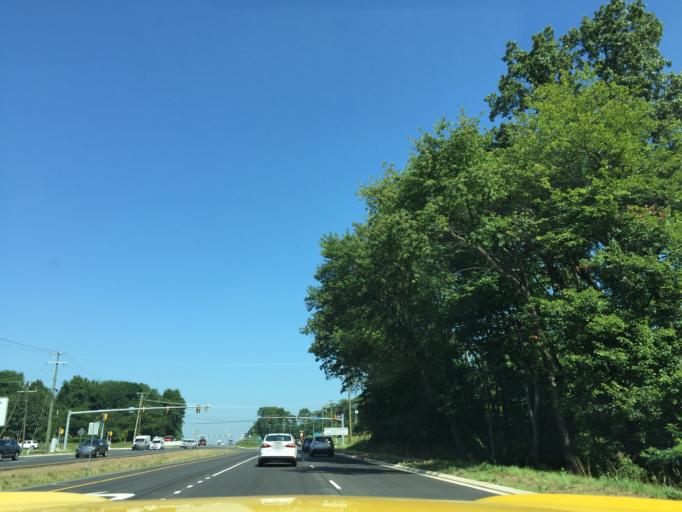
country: US
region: Virginia
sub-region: Fairfax County
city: Dranesville
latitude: 38.9983
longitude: -77.3414
